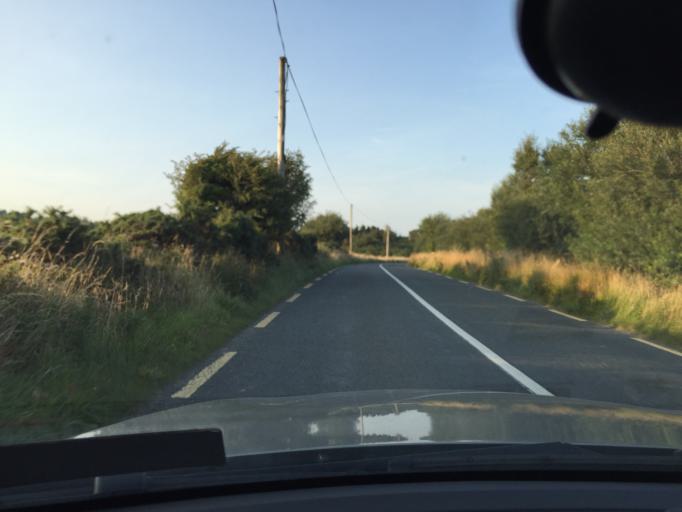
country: IE
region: Leinster
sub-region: Wicklow
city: Rathdrum
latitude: 53.0553
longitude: -6.2366
